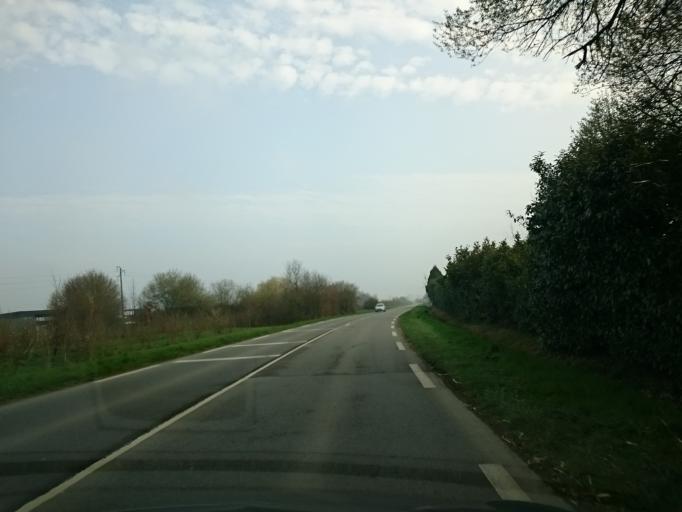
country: FR
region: Brittany
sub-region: Departement d'Ille-et-Vilaine
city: Chatillon-sur-Seiche
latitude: 48.0706
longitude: -1.6655
